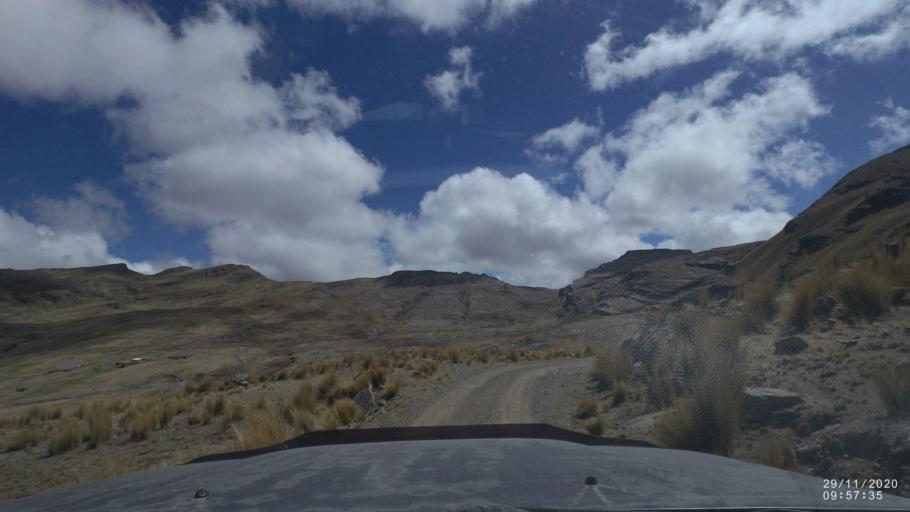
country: BO
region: Cochabamba
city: Cochabamba
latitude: -17.2702
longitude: -66.1691
